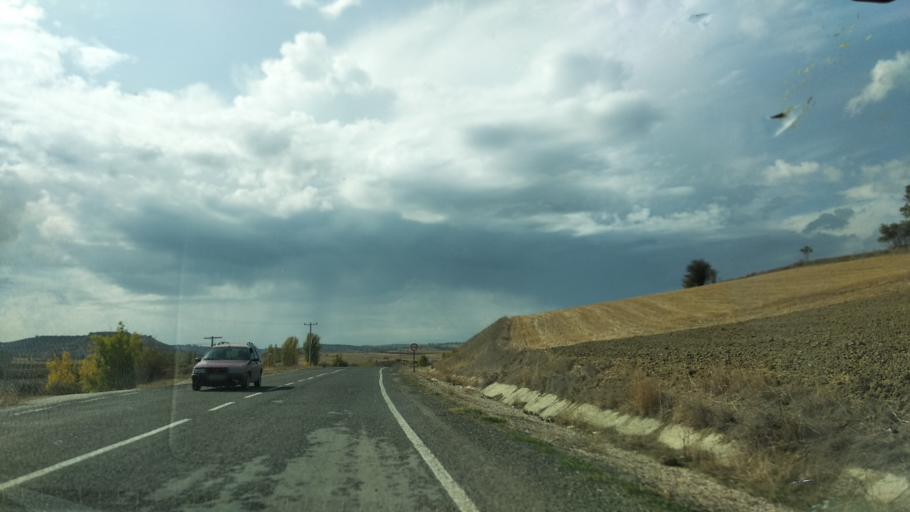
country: TR
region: Bolu
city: Seben
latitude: 40.3990
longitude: 31.5594
